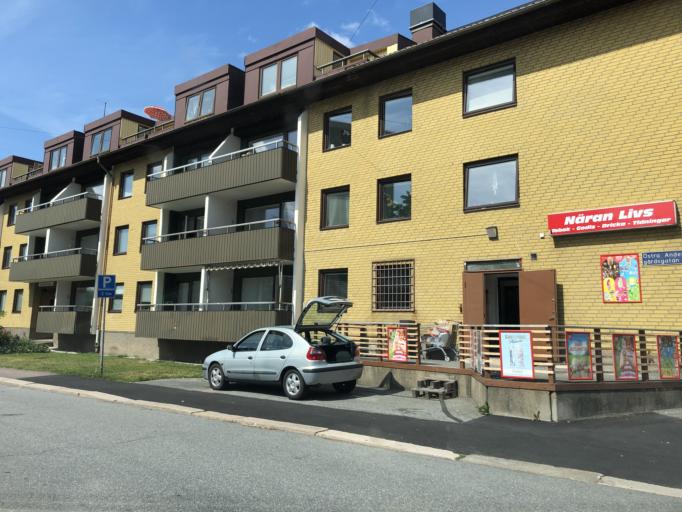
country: SE
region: Vaestra Goetaland
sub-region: Goteborg
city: Majorna
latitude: 57.7155
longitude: 11.9289
